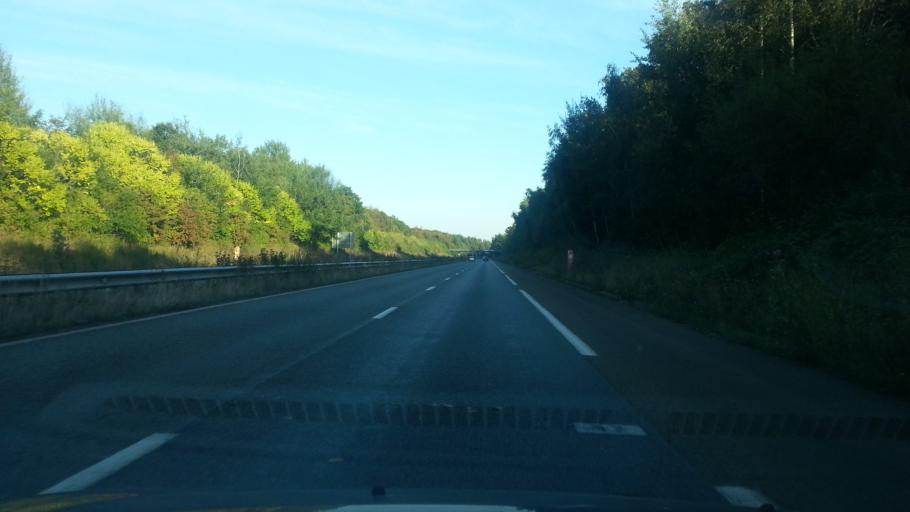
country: FR
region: Picardie
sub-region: Departement de l'Oise
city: Agnetz
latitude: 49.4073
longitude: 2.3528
